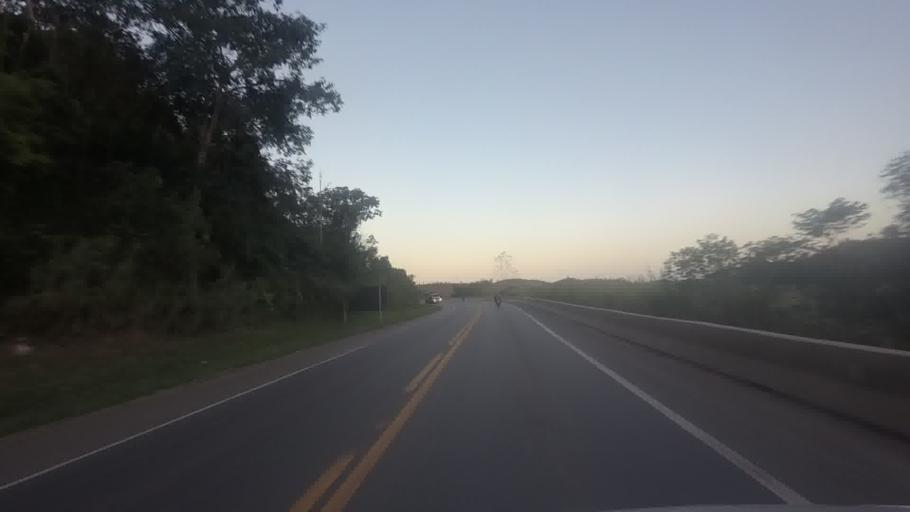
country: BR
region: Espirito Santo
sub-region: Rio Novo Do Sul
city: Rio Novo do Sul
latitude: -20.8756
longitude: -40.9571
